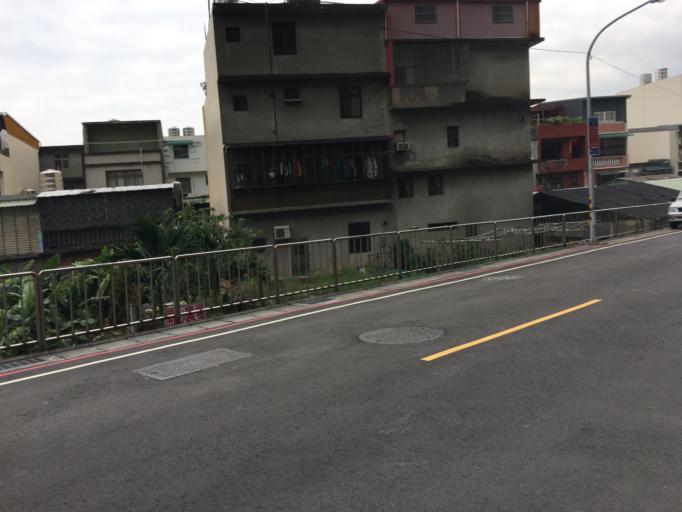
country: TW
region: Taiwan
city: Taoyuan City
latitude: 25.0180
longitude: 121.3057
